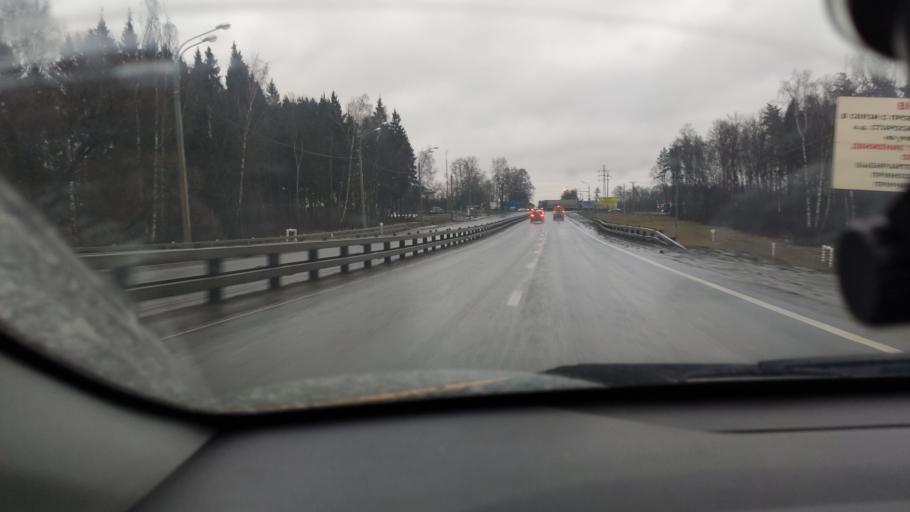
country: RU
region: Moskovskaya
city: Dubrovitsy
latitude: 55.3749
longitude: 37.3933
